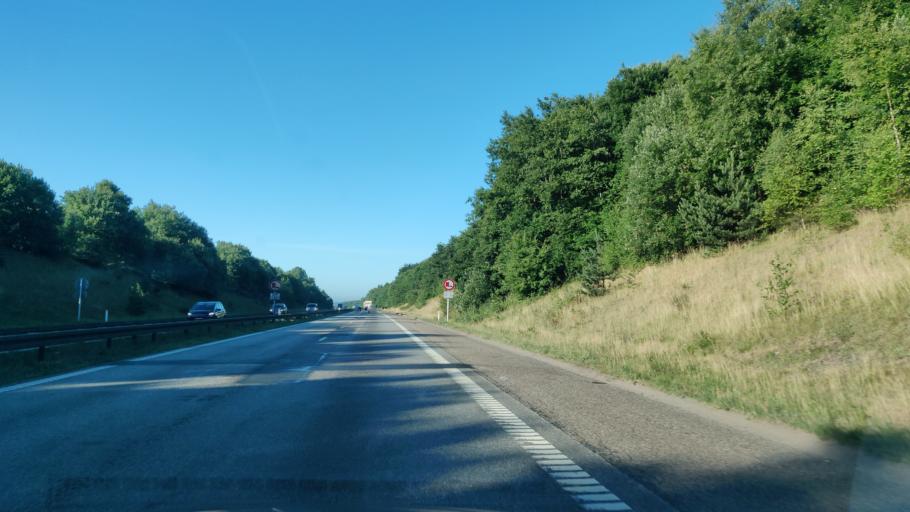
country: DK
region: North Denmark
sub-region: Rebild Kommune
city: Stovring
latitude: 56.9251
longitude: 9.8455
